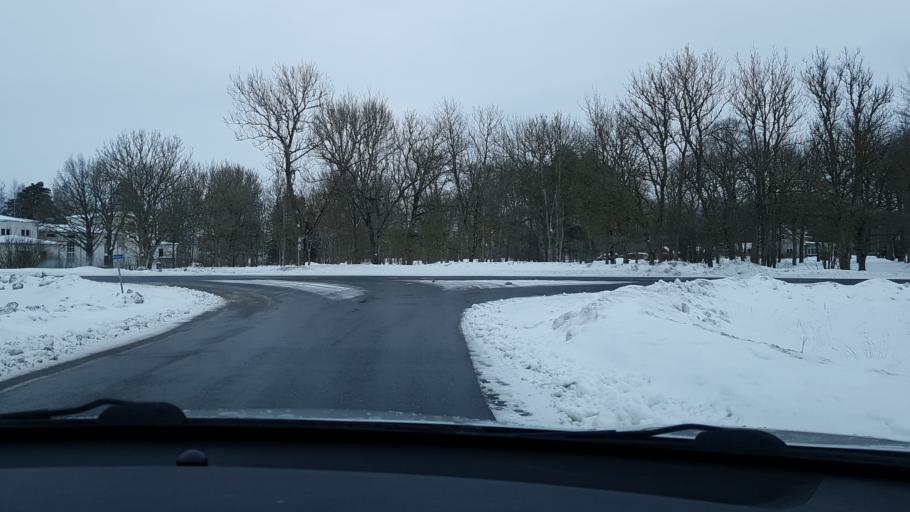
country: EE
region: Jaervamaa
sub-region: Jaerva-Jaani vald
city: Jarva-Jaani
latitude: 59.1397
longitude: 25.7535
